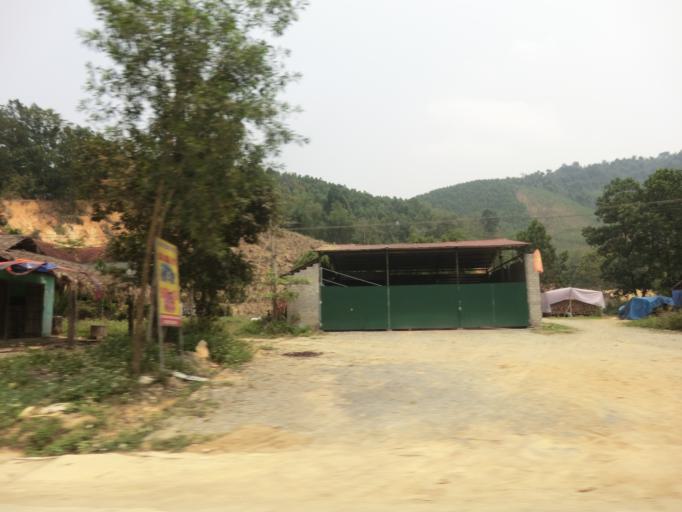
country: VN
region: Thanh Hoa
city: Thi Tran Thuong Xuan
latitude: 19.7913
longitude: 105.3995
